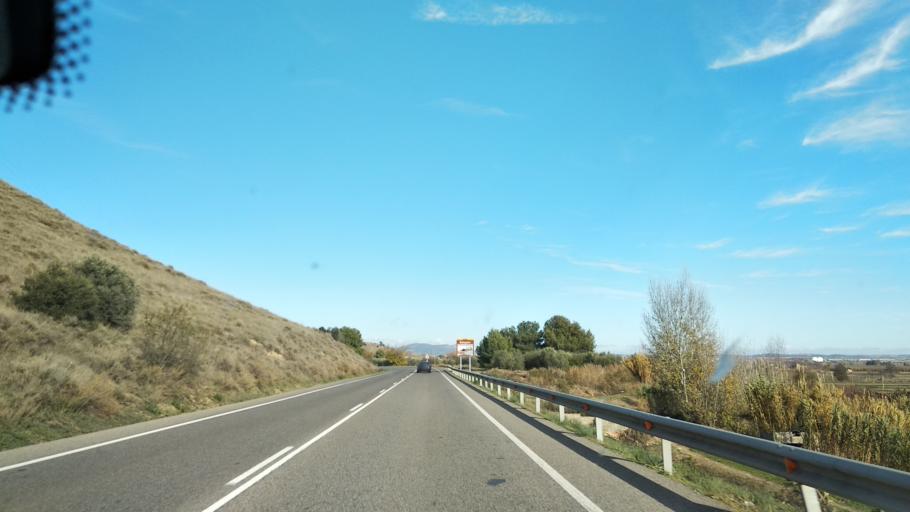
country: ES
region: Catalonia
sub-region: Provincia de Lleida
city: Termens
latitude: 41.7578
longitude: 0.7725
